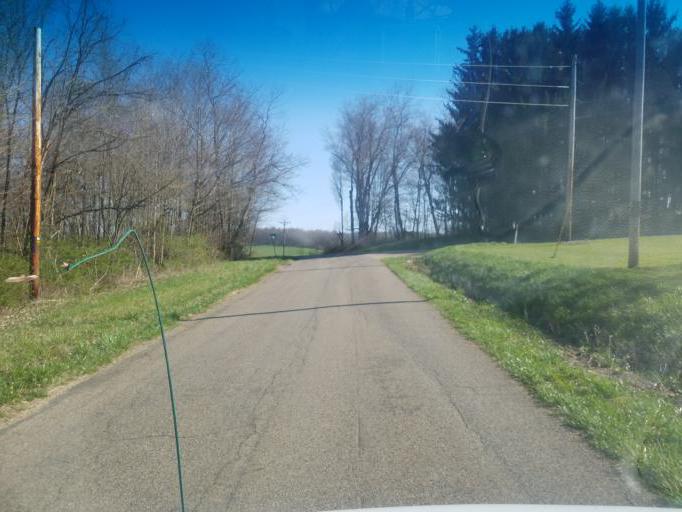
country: US
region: Ohio
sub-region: Knox County
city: Oak Hill
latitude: 40.2625
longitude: -82.2234
